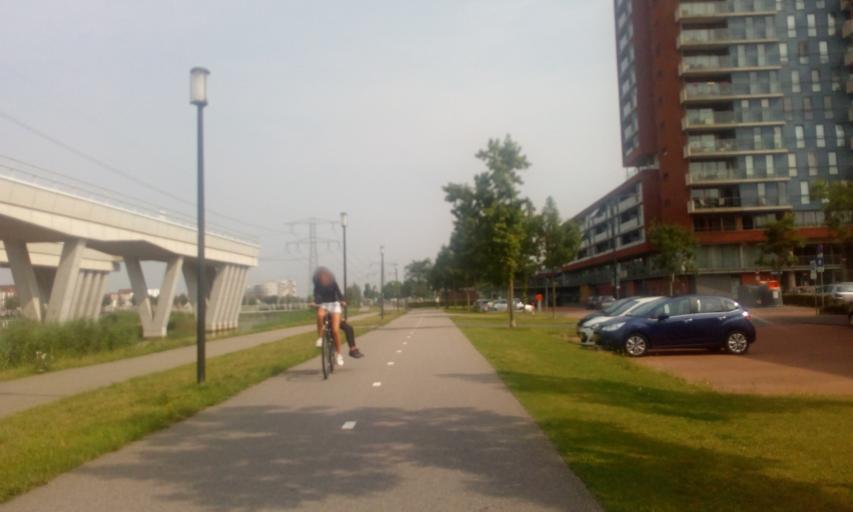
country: NL
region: South Holland
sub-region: Gemeente Capelle aan den IJssel
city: Capelle aan den IJssel
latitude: 51.9807
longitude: 4.5872
